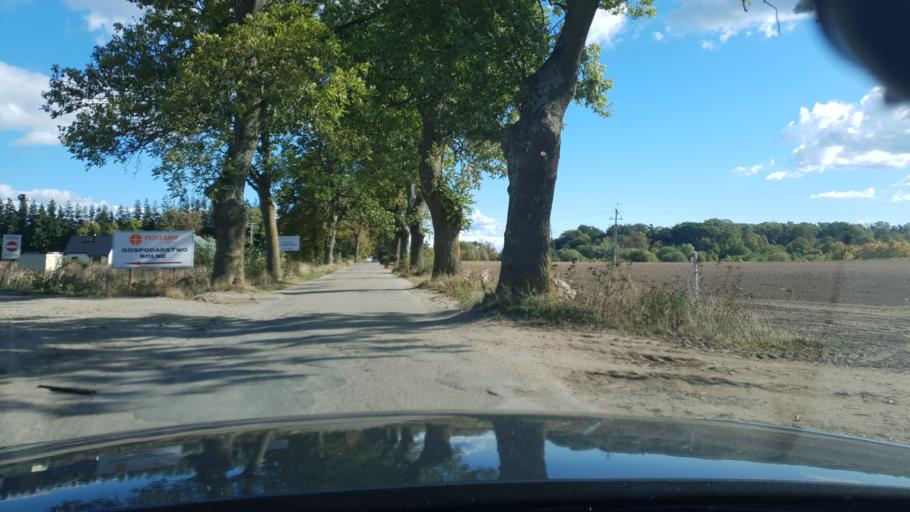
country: PL
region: Pomeranian Voivodeship
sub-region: Powiat pucki
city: Zelistrzewo
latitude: 54.6864
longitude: 18.4560
